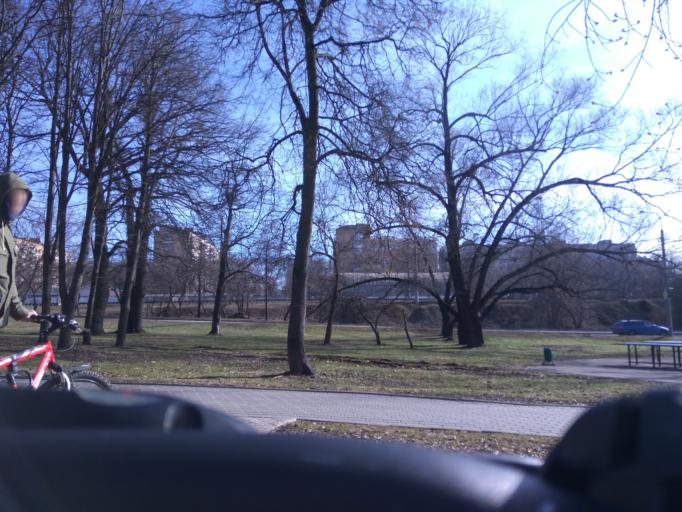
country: RU
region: Moskovskaya
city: Bol'shaya Setun'
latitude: 55.7276
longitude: 37.4401
